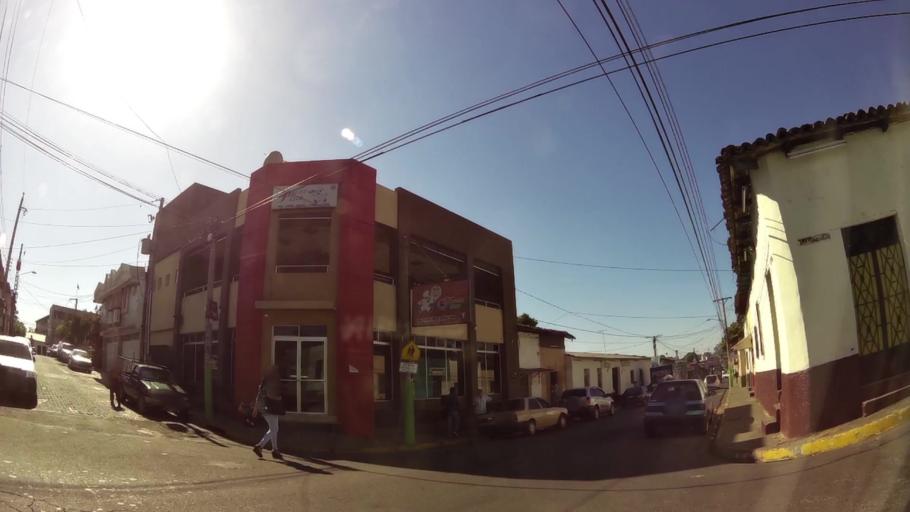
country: SV
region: Sonsonate
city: Sonsonate
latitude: 13.7249
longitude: -89.7245
